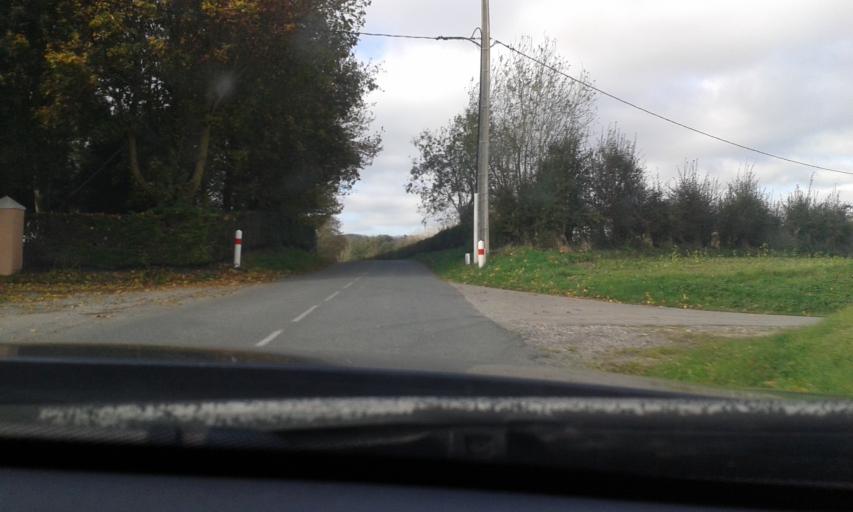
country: FR
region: Nord-Pas-de-Calais
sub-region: Departement du Pas-de-Calais
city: Hames-Boucres
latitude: 50.8696
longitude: 1.8058
